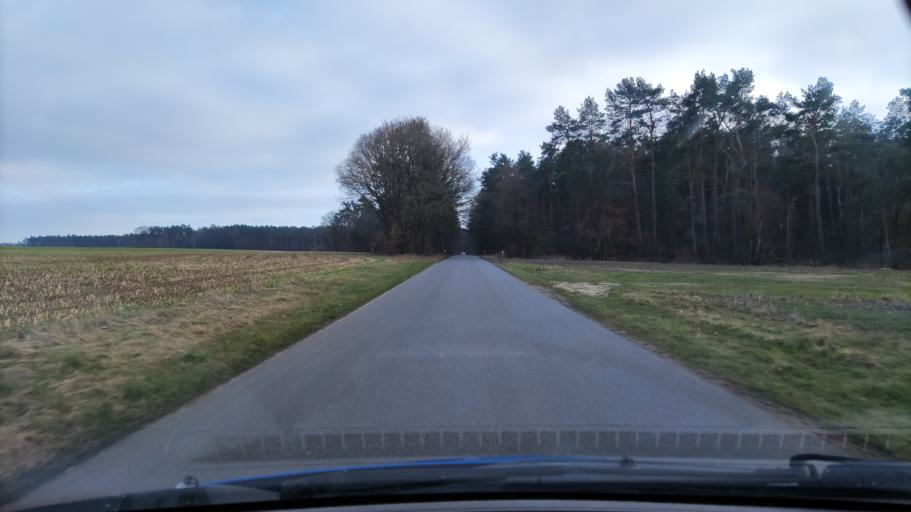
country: DE
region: Lower Saxony
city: Gerdau
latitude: 52.9500
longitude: 10.4275
